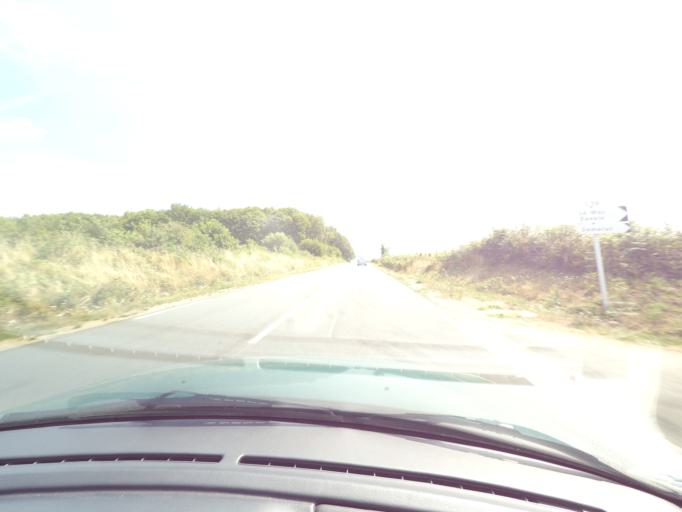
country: FR
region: Limousin
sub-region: Departement de la Haute-Vienne
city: Neuvic-Entier
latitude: 45.7292
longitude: 1.6506
